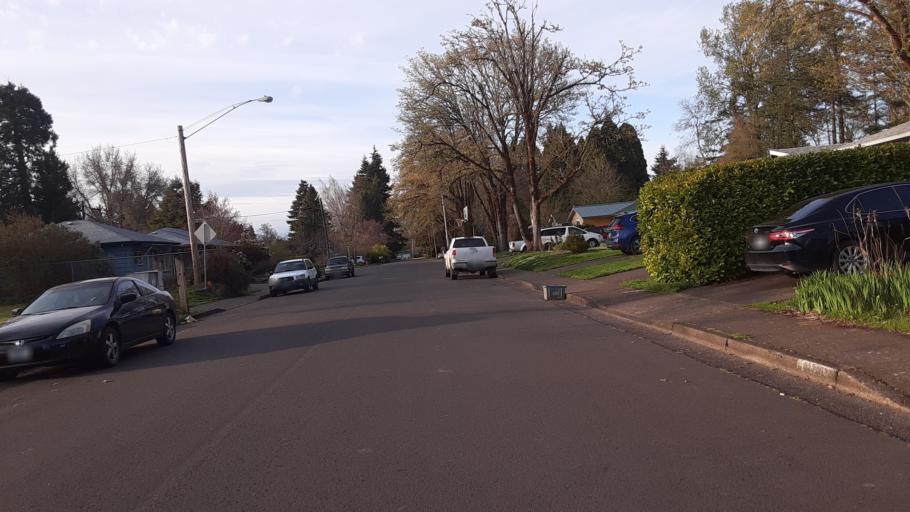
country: US
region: Oregon
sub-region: Benton County
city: Corvallis
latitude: 44.5486
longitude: -123.2587
